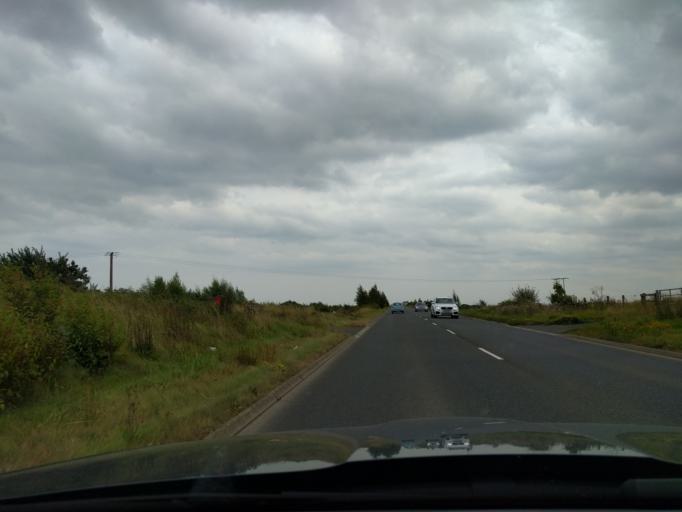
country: GB
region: England
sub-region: Northumberland
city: Pegswood
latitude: 55.1771
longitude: -1.6627
